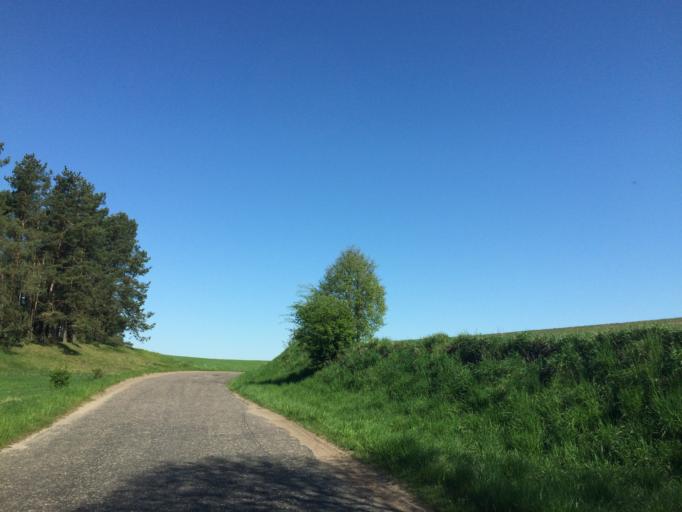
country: PL
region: Warmian-Masurian Voivodeship
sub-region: Powiat dzialdowski
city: Rybno
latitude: 53.4392
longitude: 19.9214
